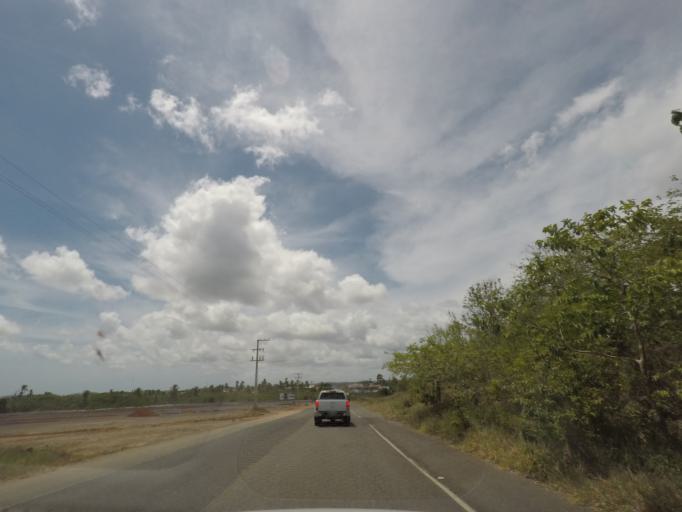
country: BR
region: Sergipe
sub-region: Indiaroba
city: Indiaroba
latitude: -11.5128
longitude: -37.5099
